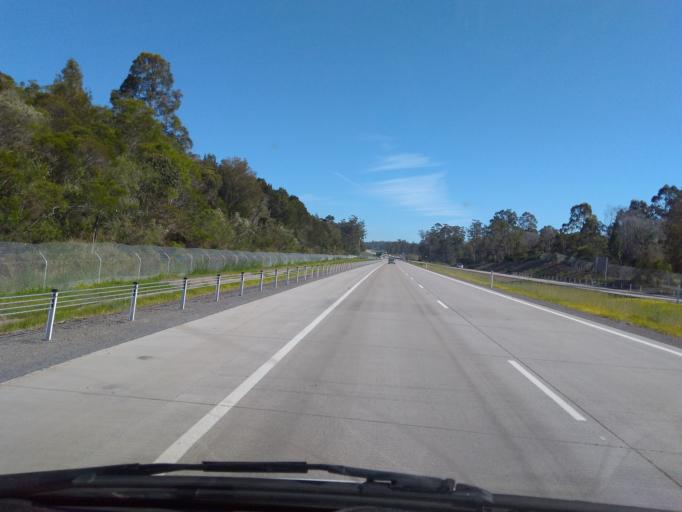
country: AU
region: New South Wales
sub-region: Kempsey
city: Kempsey
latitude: -31.2014
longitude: 152.8230
